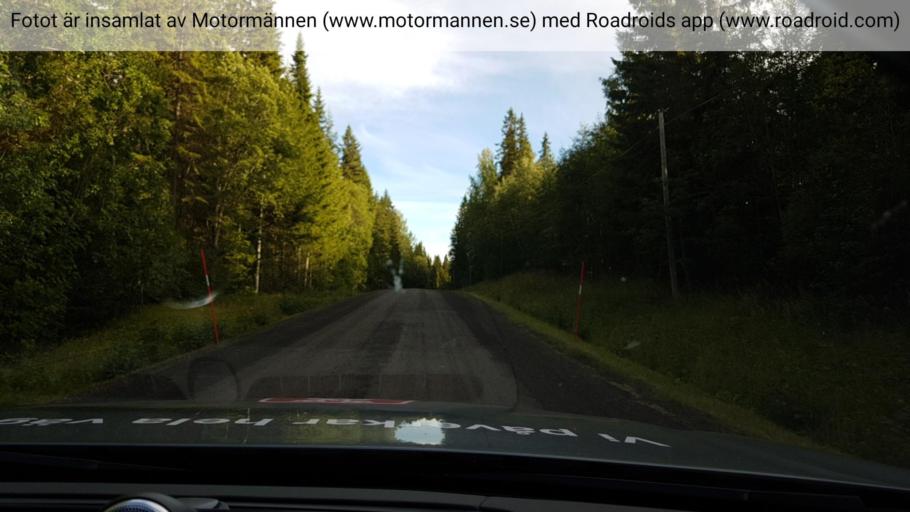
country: SE
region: Jaemtland
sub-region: Stroemsunds Kommun
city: Stroemsund
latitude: 64.1029
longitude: 15.8224
